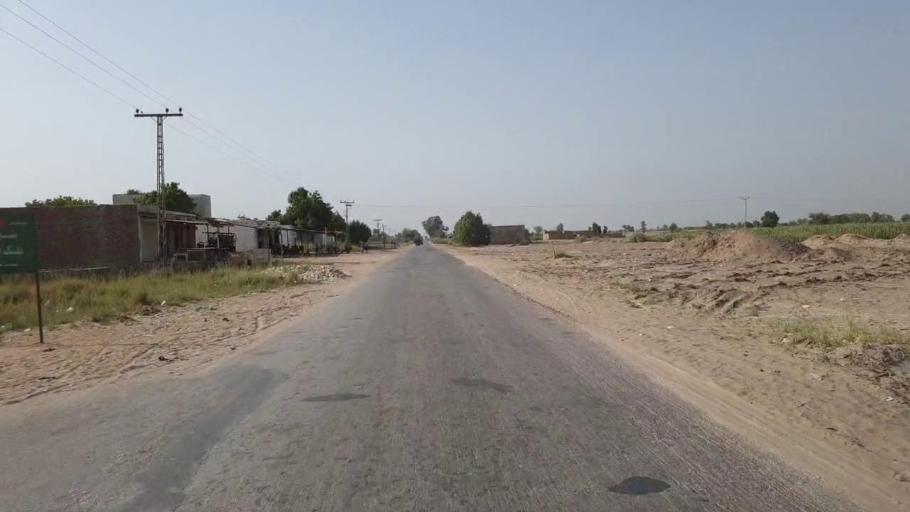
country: PK
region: Sindh
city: Sanghar
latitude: 26.2863
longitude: 68.9308
